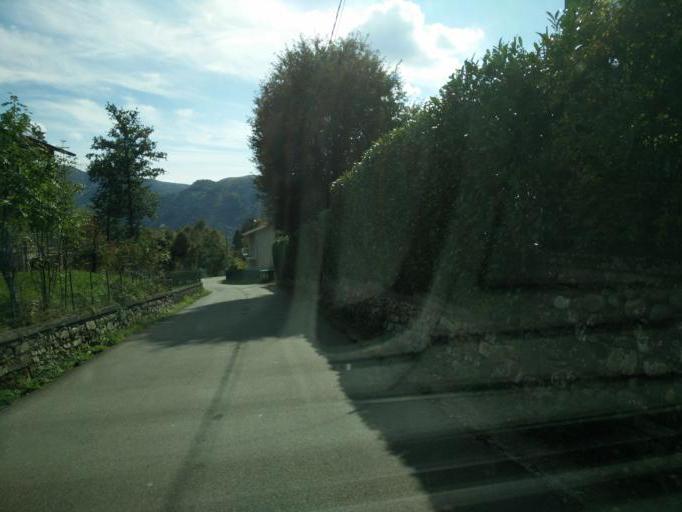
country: IT
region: Tuscany
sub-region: Provincia di Massa-Carrara
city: Zeri
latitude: 44.3554
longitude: 9.7613
